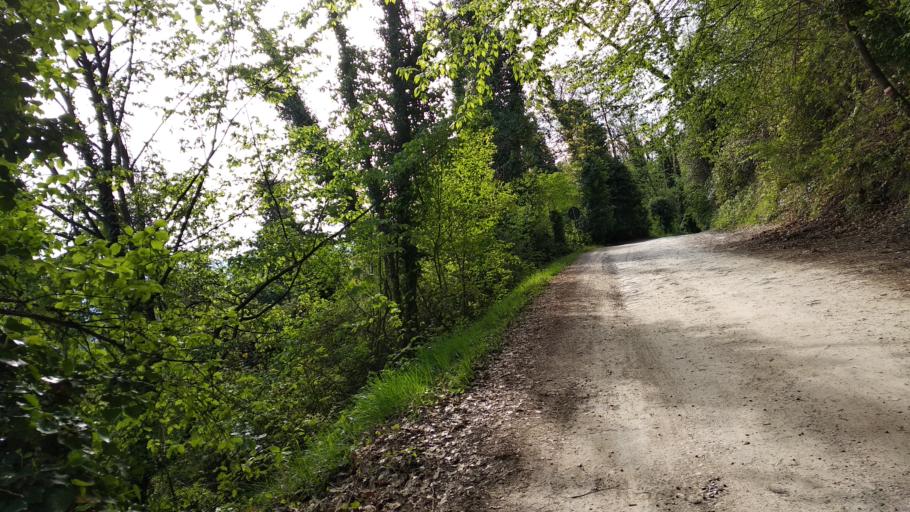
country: IT
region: Emilia-Romagna
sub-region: Provincia di Ravenna
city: Fognano
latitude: 44.2267
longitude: 11.7430
